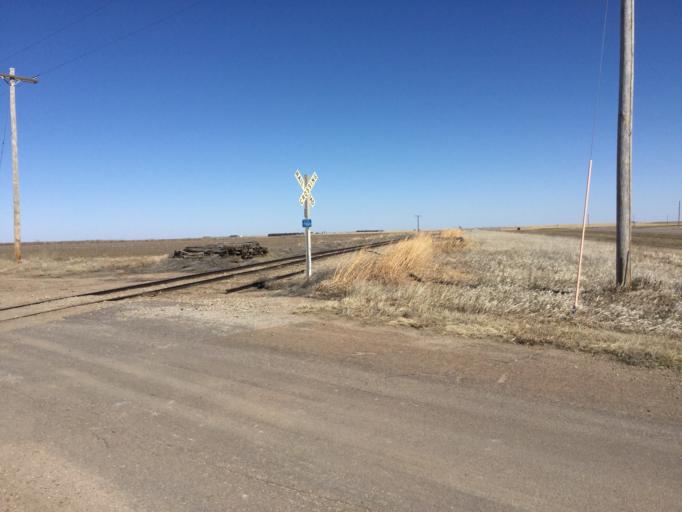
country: US
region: Kansas
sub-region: Sheridan County
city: Hoxie
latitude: 39.4944
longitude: -100.6834
